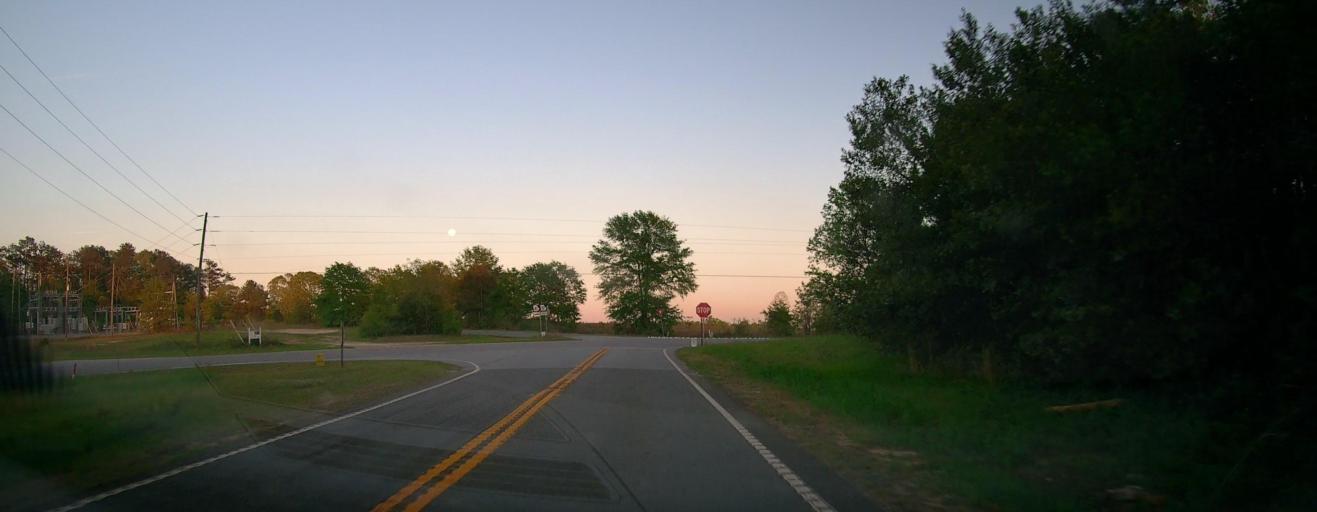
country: US
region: Georgia
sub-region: Marion County
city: Buena Vista
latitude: 32.3676
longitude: -84.5406
